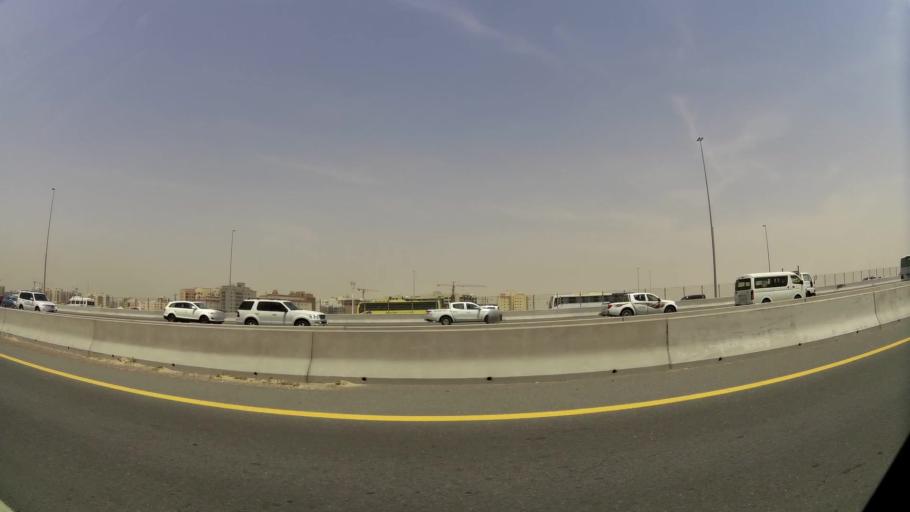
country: AE
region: Ash Shariqah
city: Sharjah
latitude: 25.1824
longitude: 55.3968
